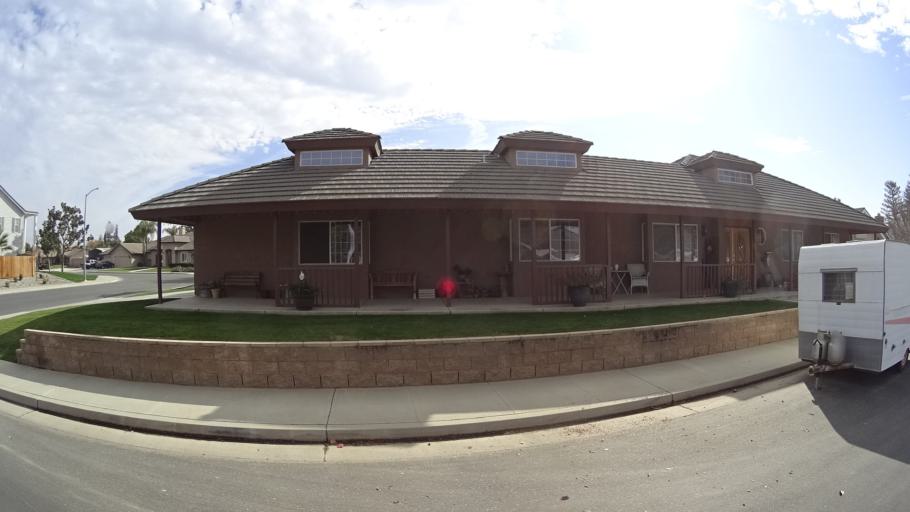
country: US
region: California
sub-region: Kern County
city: Greenacres
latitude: 35.4093
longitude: -119.1256
